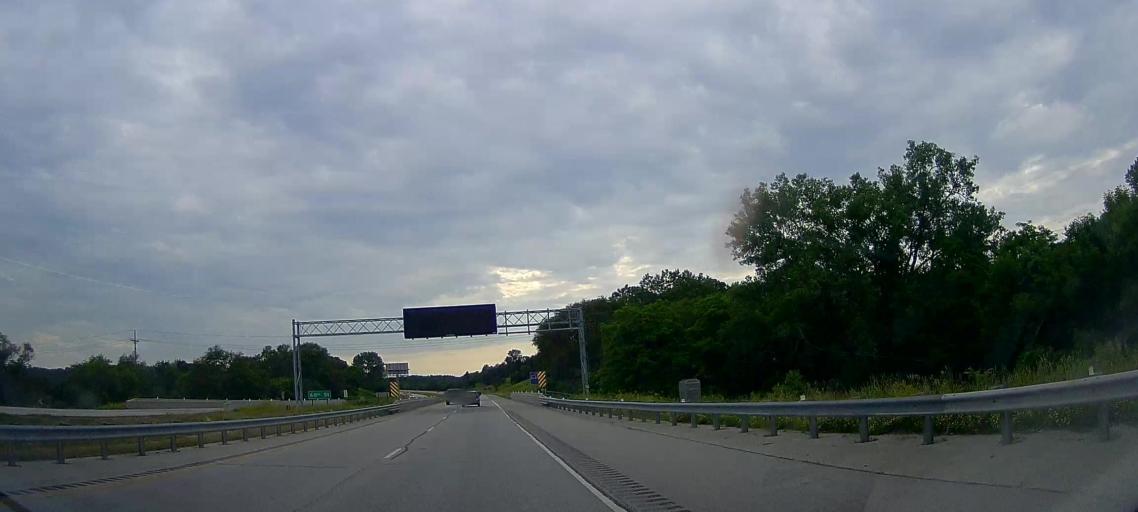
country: US
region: Iowa
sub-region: Pottawattamie County
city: Carter Lake
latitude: 41.3463
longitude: -96.0042
